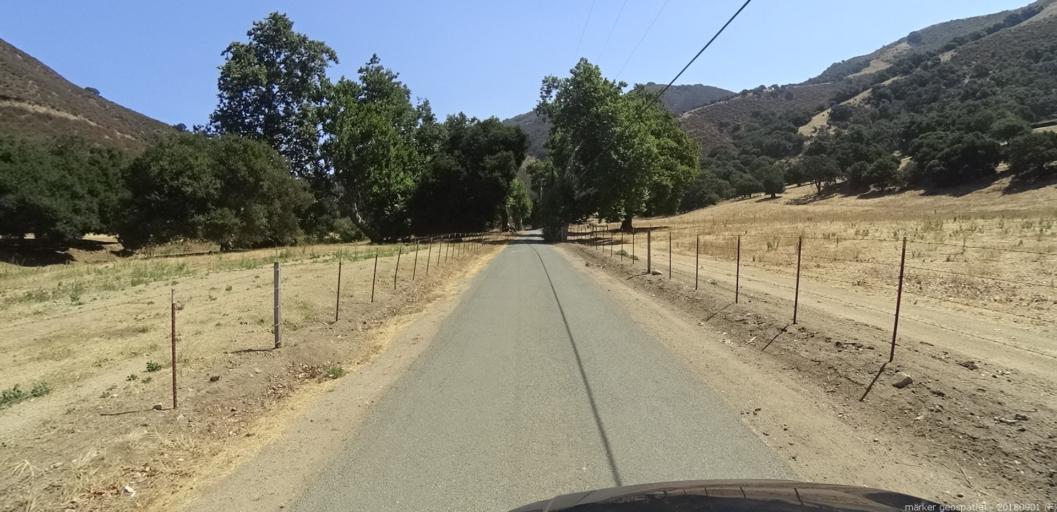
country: US
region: California
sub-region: Monterey County
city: Gonzales
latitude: 36.6039
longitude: -121.4042
